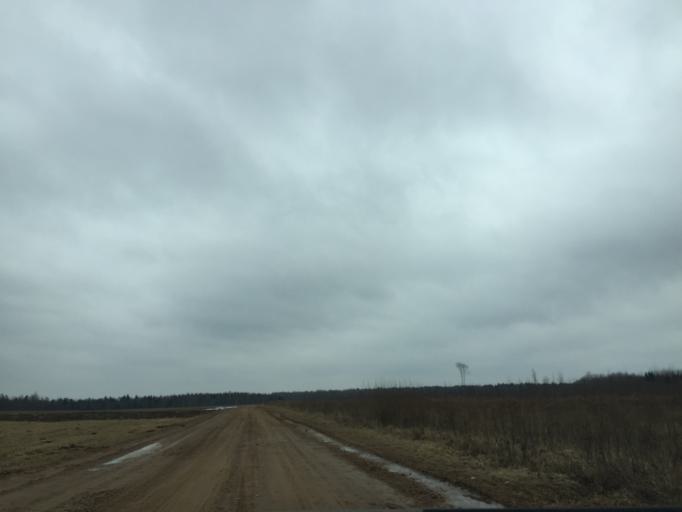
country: LV
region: Lielvarde
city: Lielvarde
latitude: 56.7575
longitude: 24.8040
